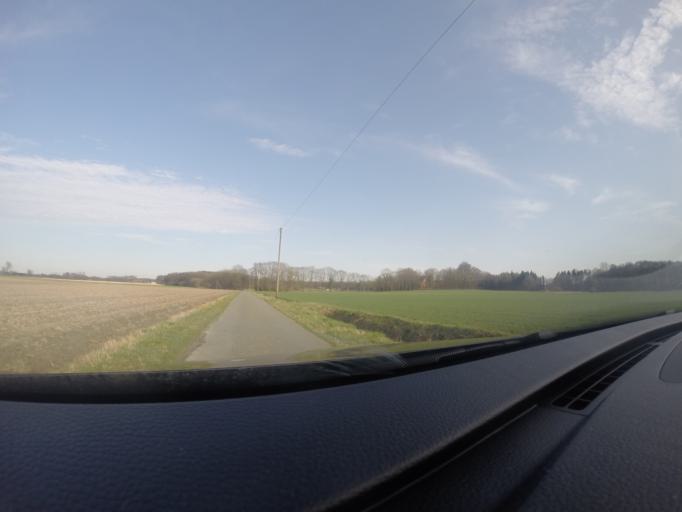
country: DE
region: North Rhine-Westphalia
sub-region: Regierungsbezirk Munster
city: Horstmar
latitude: 52.0953
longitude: 7.3313
